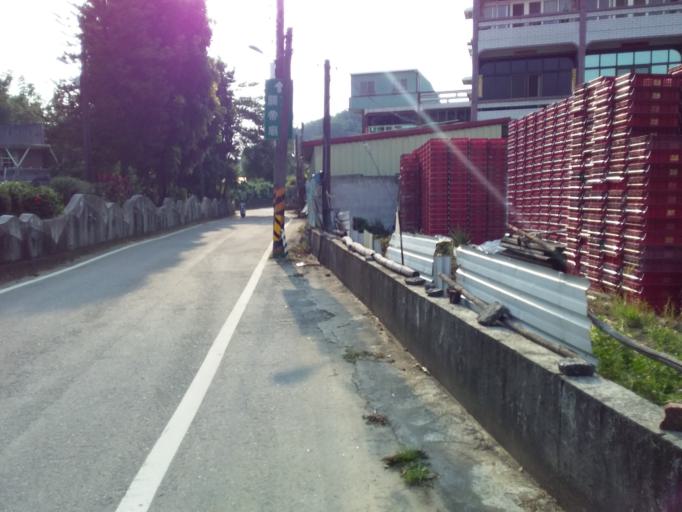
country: TW
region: Taiwan
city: Fengshan
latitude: 22.6891
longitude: 120.4089
